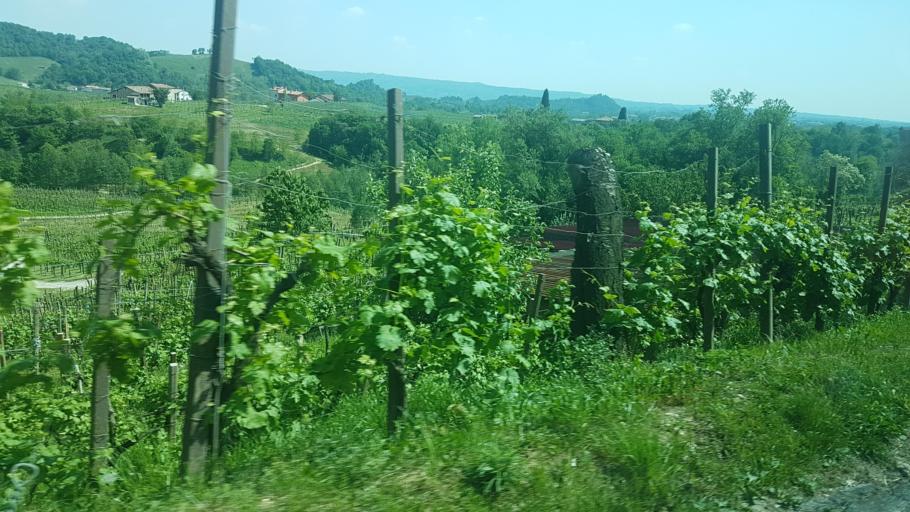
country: IT
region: Veneto
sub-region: Provincia di Treviso
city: Bigolino
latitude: 45.8962
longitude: 12.0254
